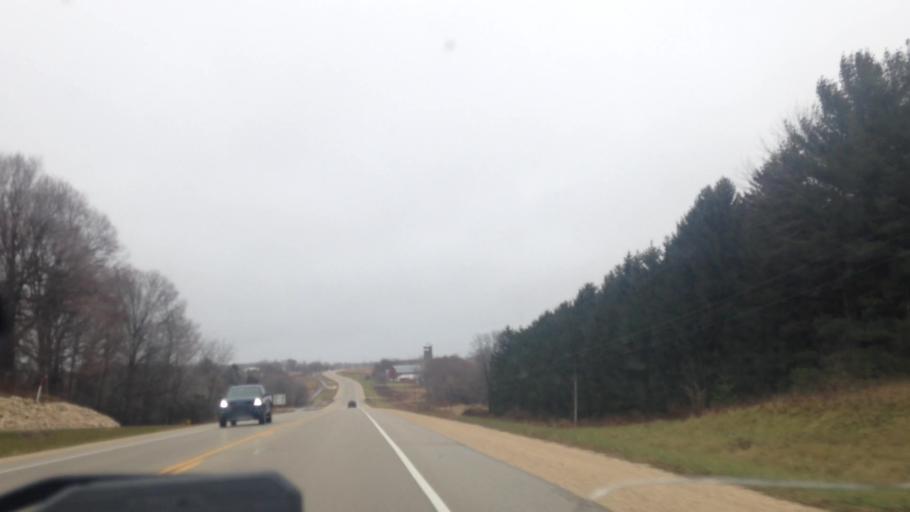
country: US
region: Wisconsin
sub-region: Dodge County
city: Horicon
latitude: 43.4769
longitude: -88.5935
